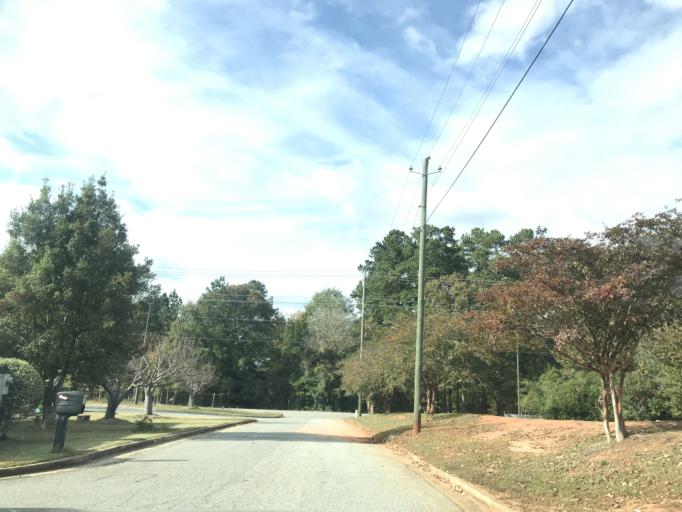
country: US
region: Georgia
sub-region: Jones County
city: Gray
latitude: 33.0049
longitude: -83.5489
